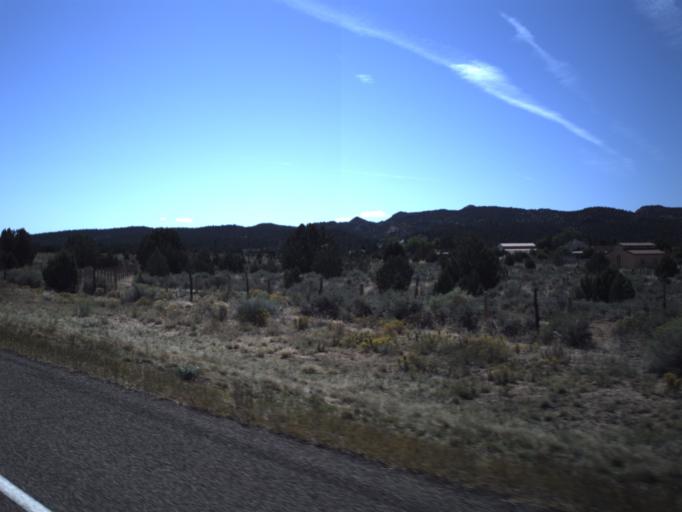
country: US
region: Utah
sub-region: Washington County
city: Ivins
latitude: 37.2993
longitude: -113.6663
